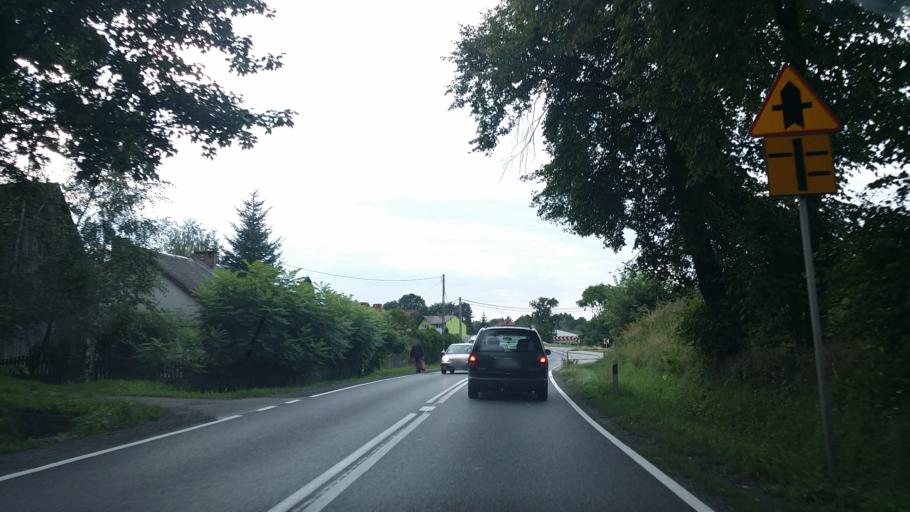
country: PL
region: Lesser Poland Voivodeship
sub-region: Powiat oswiecimski
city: Przeciszow
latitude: 50.0043
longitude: 19.3985
